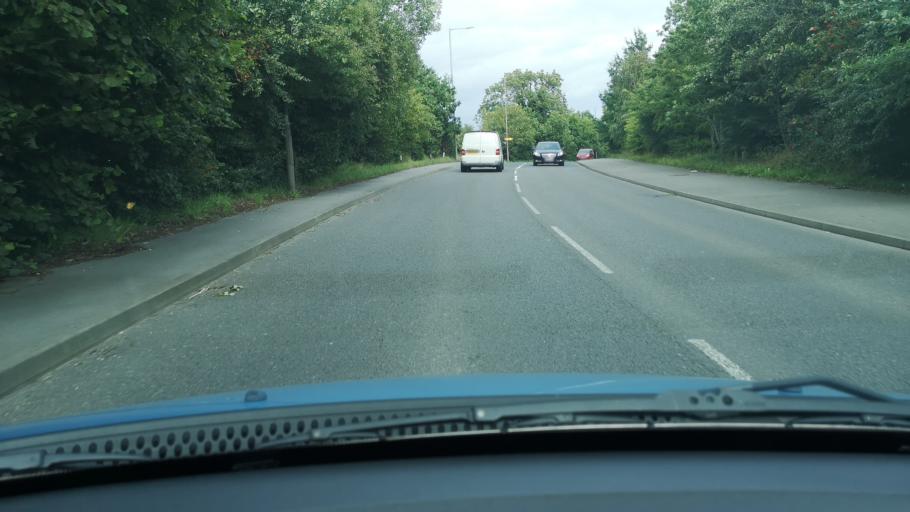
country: GB
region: England
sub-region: Barnsley
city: Shafton
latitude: 53.5924
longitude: -1.3979
